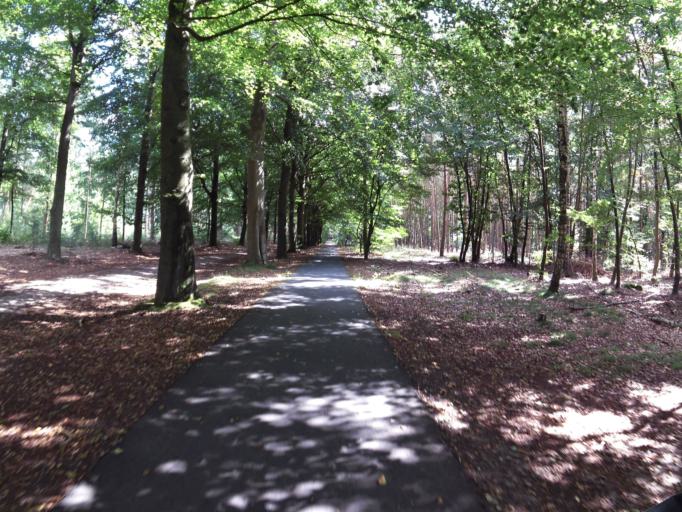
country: NL
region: Drenthe
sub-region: Gemeente Aa en Hunze
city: Anloo
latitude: 52.9877
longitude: 6.7176
